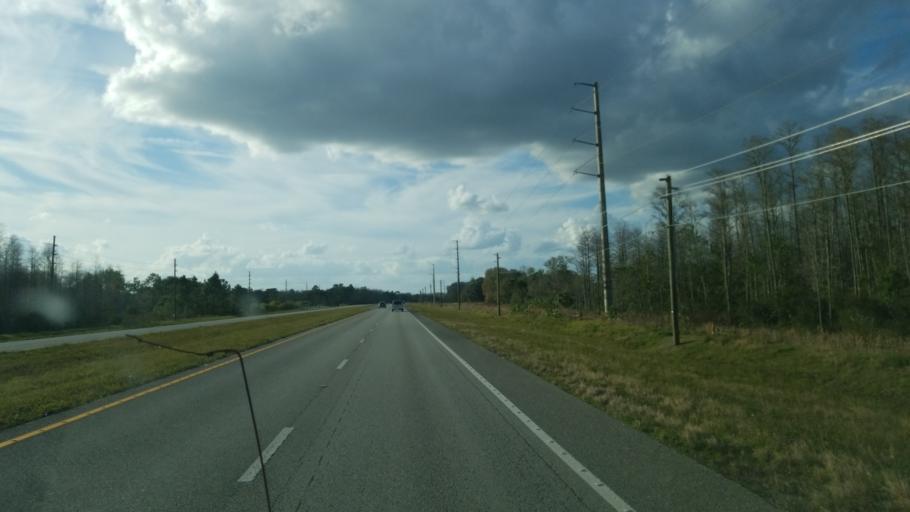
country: US
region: Florida
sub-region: Osceola County
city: Saint Cloud
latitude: 28.1477
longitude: -81.0956
